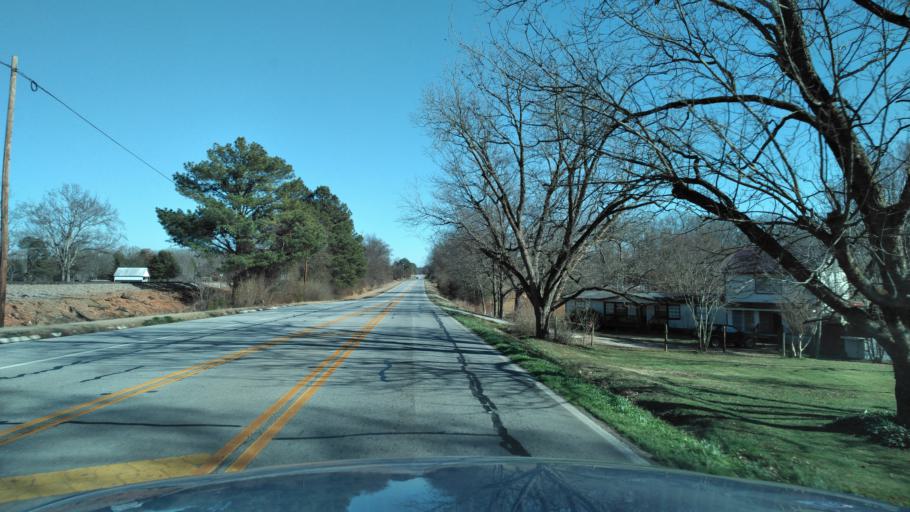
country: US
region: Georgia
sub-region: Banks County
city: Maysville
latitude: 34.2428
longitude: -83.5365
